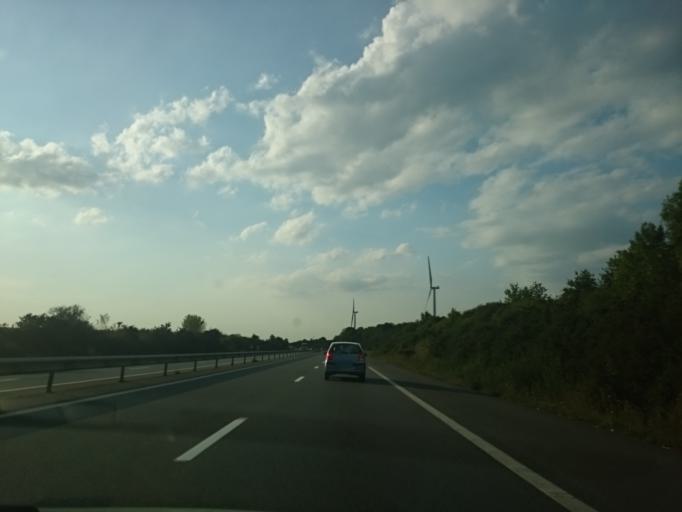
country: FR
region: Pays de la Loire
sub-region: Departement de la Loire-Atlantique
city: Prinquiau
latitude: 47.4084
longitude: -2.0157
